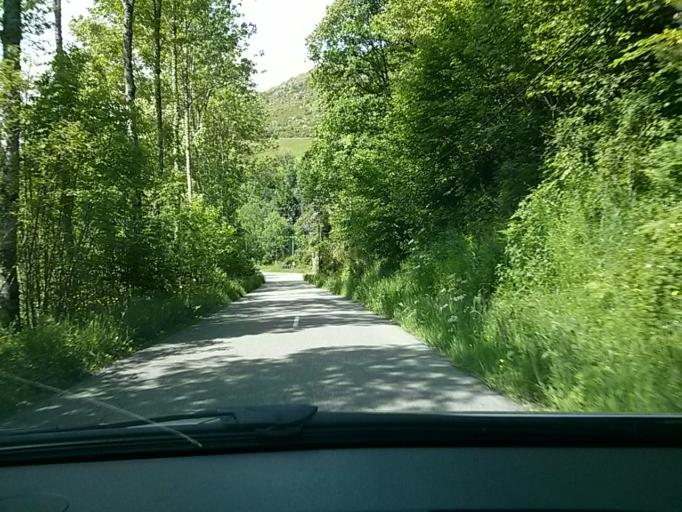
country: FR
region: Rhone-Alpes
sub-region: Departement de la Loire
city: Saint-Chamond
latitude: 45.4098
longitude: 4.5396
